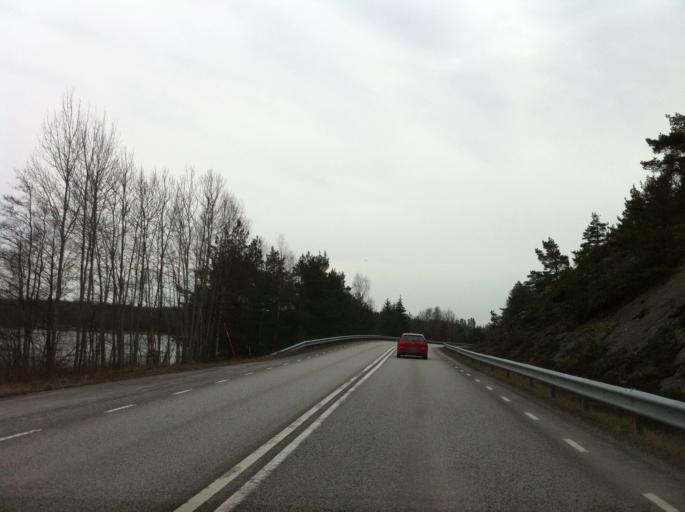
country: SE
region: Vaestra Goetaland
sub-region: Orust
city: Henan
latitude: 58.2736
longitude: 11.6938
